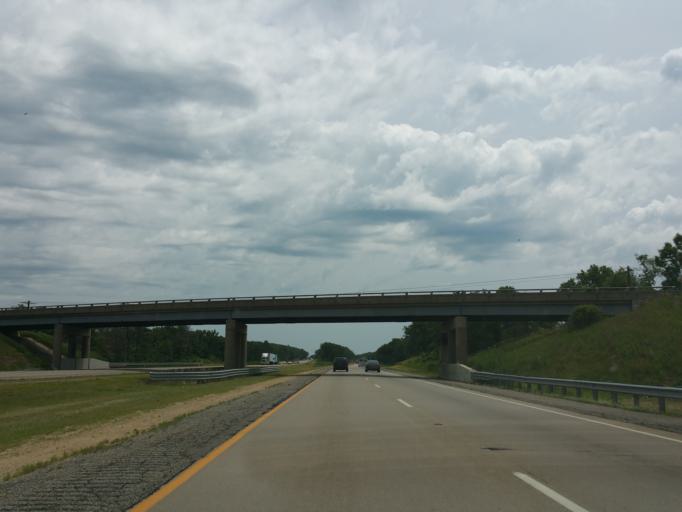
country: US
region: Wisconsin
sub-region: Columbia County
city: Wisconsin Dells
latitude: 43.6813
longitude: -89.8374
